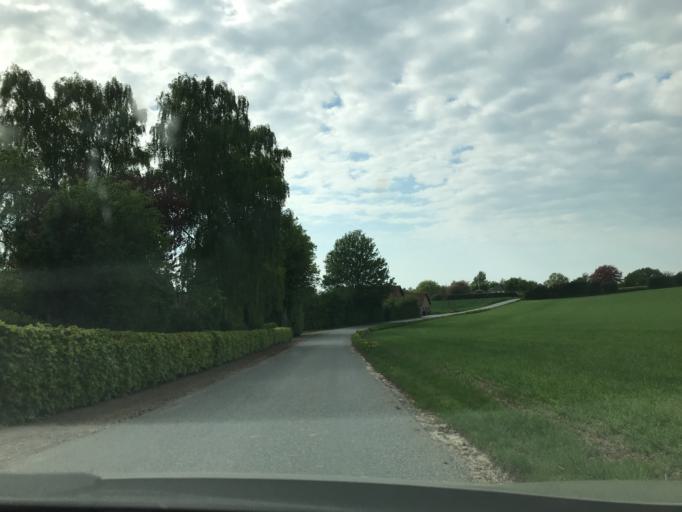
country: DK
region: South Denmark
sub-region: Middelfart Kommune
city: Ejby
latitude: 55.3560
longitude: 9.8857
